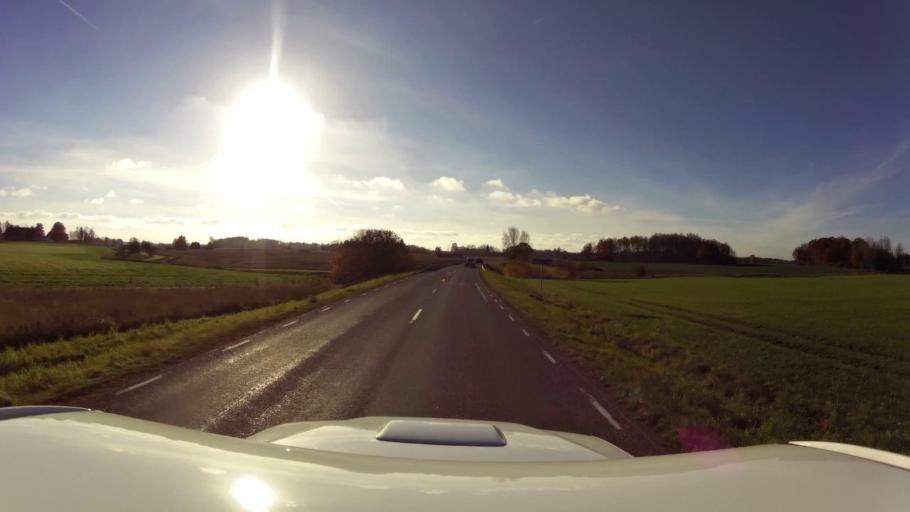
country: SE
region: OEstergoetland
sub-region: Linkopings Kommun
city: Malmslatt
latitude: 58.3500
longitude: 15.5453
